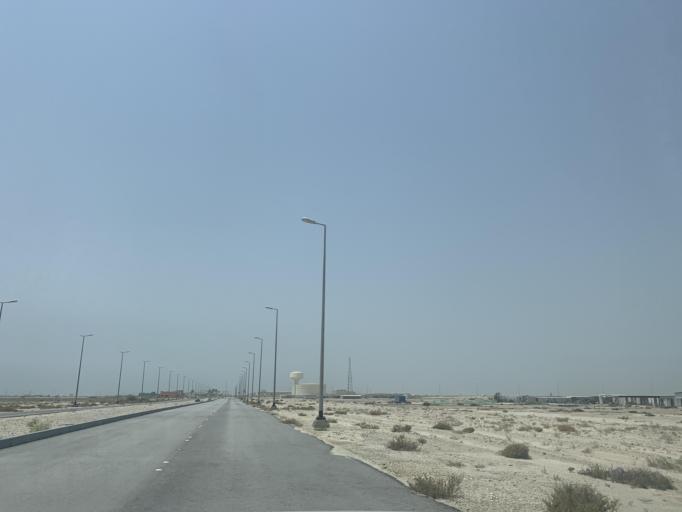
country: BH
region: Central Governorate
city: Dar Kulayb
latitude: 25.8457
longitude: 50.5903
